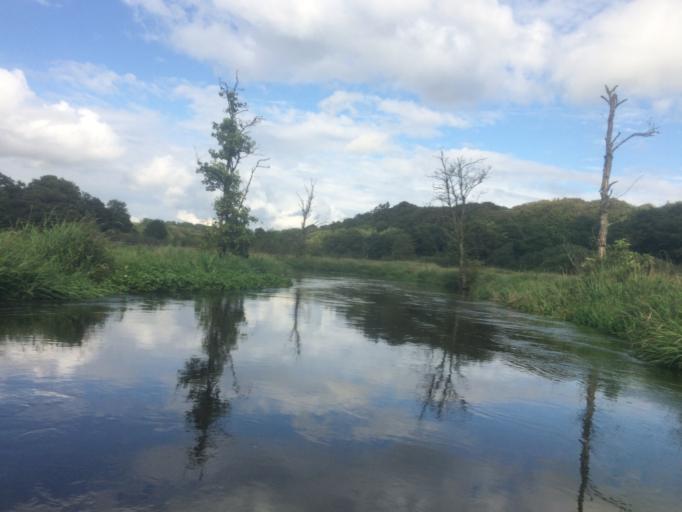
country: DK
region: South Denmark
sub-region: Vejle Kommune
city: Egtved
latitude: 55.6571
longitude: 9.3137
